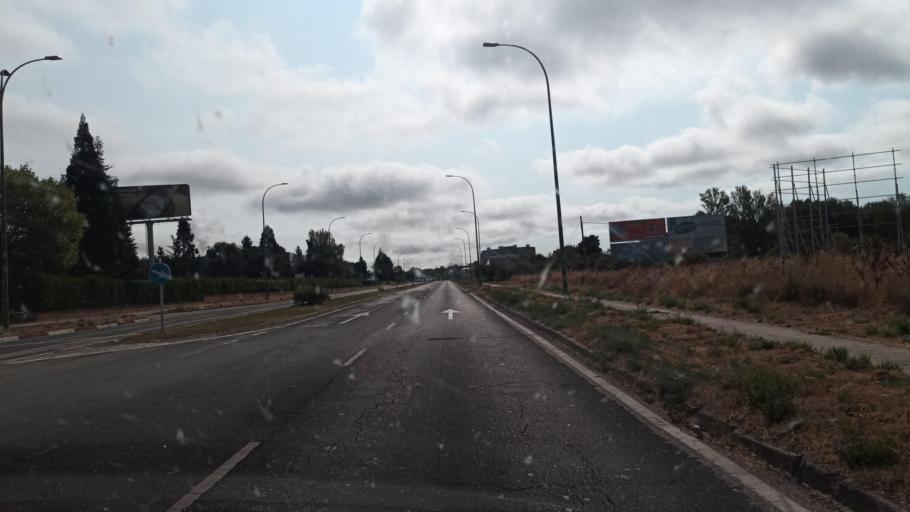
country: ES
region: Castille and Leon
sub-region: Provincia de Burgos
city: Burgos
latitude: 42.3460
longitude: -3.6587
